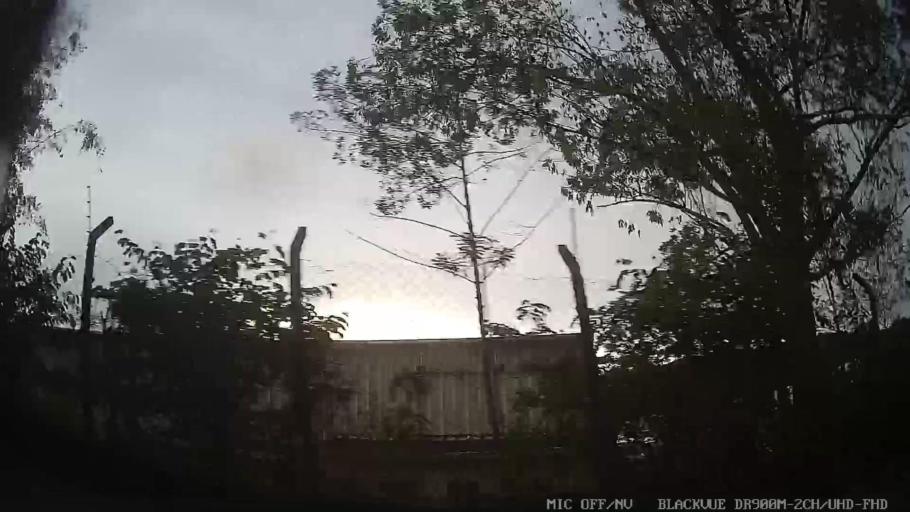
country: BR
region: Sao Paulo
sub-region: Ribeirao Pires
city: Ribeirao Pires
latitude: -23.6870
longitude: -46.3607
